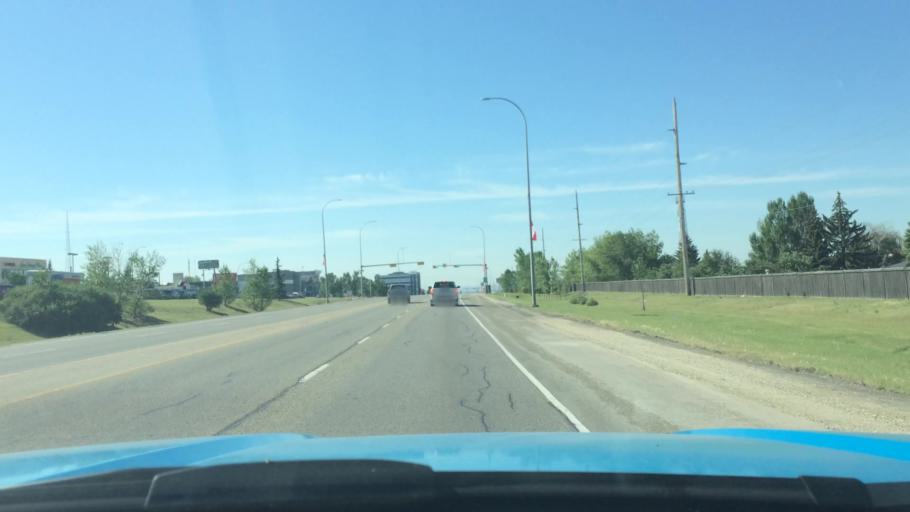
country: CA
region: Alberta
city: Calgary
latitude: 51.0571
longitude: -114.0018
